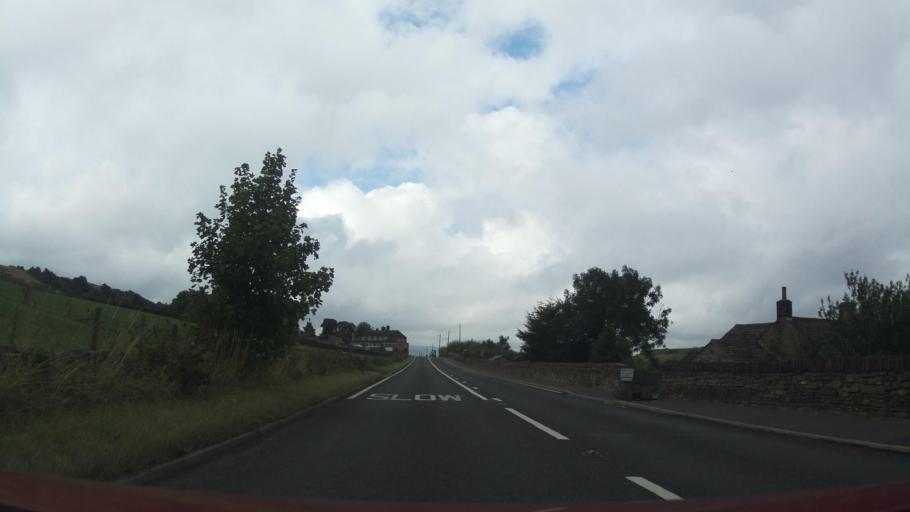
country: GB
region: England
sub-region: Kirklees
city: Kirkburton
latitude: 53.5755
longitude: -1.7227
